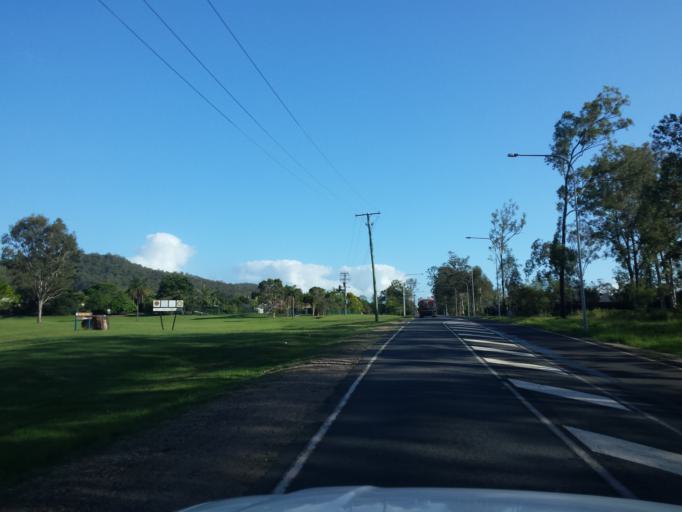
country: AU
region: Queensland
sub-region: Logan
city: Windaroo
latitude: -27.7598
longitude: 153.1856
